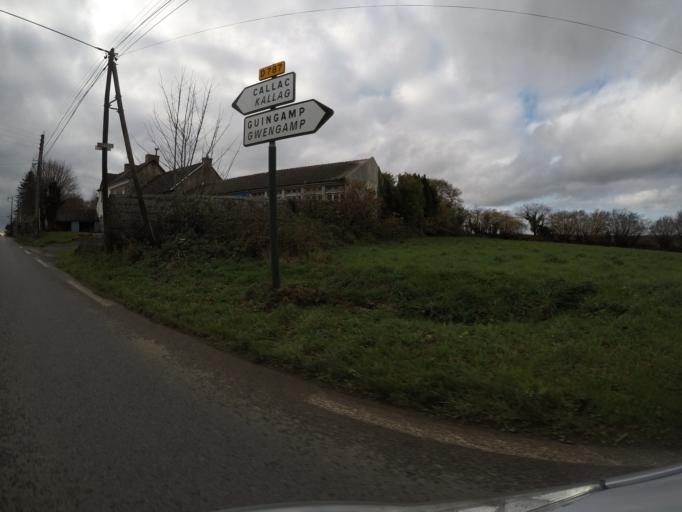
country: FR
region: Brittany
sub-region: Departement des Cotes-d'Armor
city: Callac
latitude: 48.4275
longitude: -3.3842
